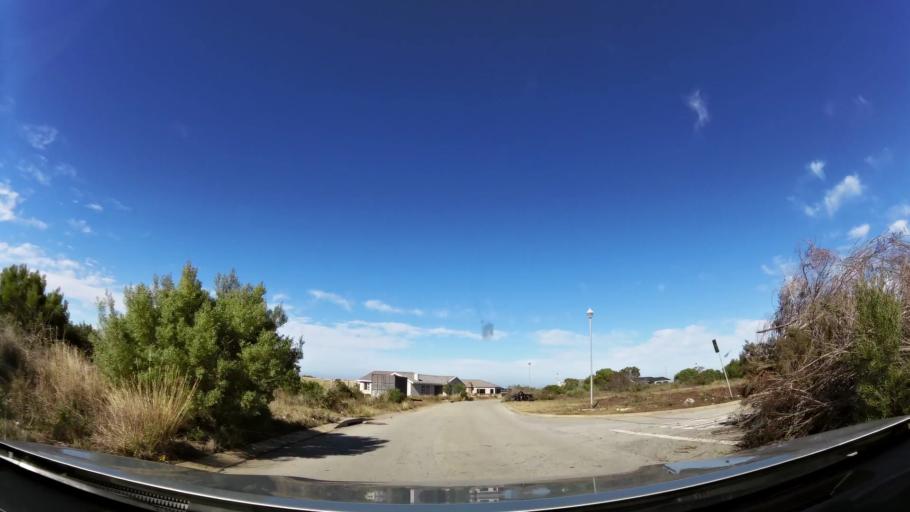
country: ZA
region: Eastern Cape
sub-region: Cacadu District Municipality
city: Jeffrey's Bay
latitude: -34.0311
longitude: 24.9034
